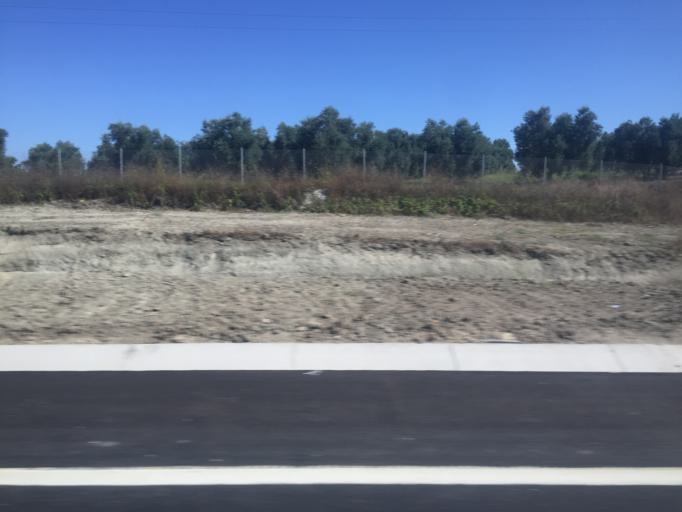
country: TR
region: Bursa
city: Gorukle
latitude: 40.2552
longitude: 28.7378
